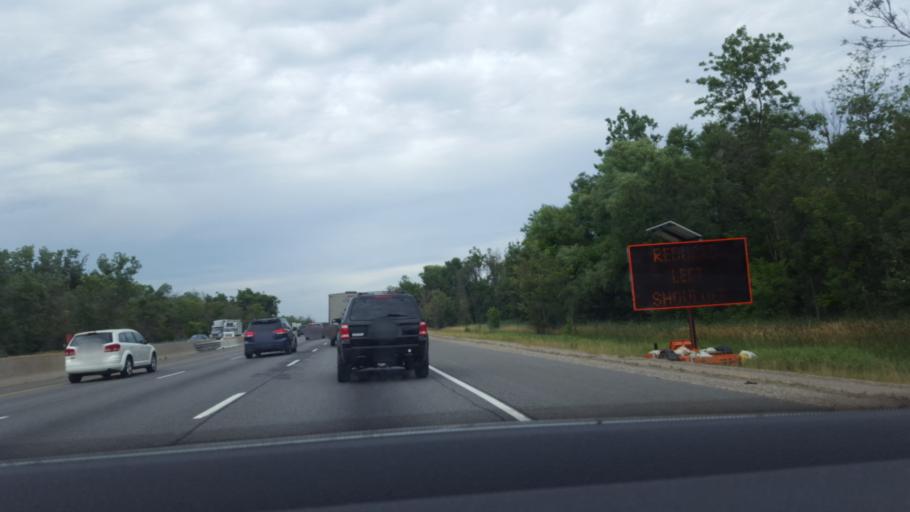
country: CA
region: Ontario
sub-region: Halton
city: Milton
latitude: 43.4852
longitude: -79.9985
